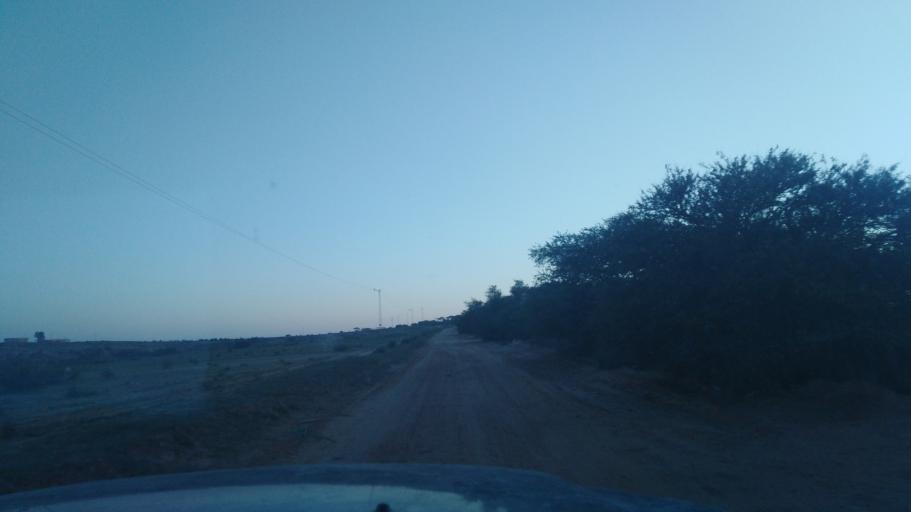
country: TN
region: Safaqis
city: Sfax
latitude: 34.7367
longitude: 10.4451
